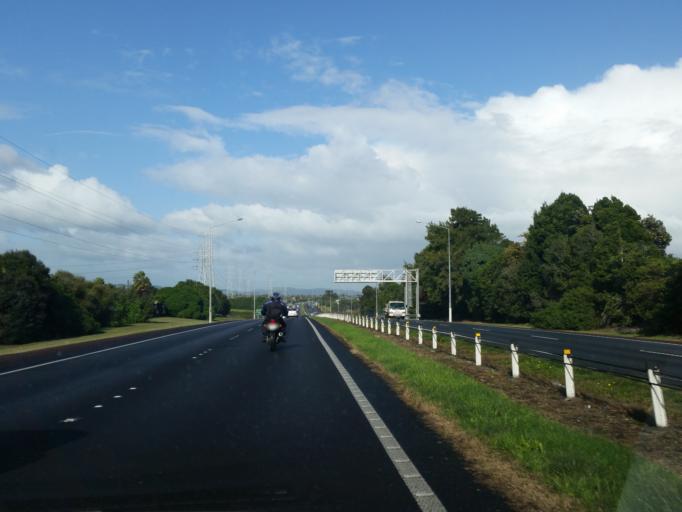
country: NZ
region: Auckland
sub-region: Auckland
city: Takanini
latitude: -37.0490
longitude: 174.9160
